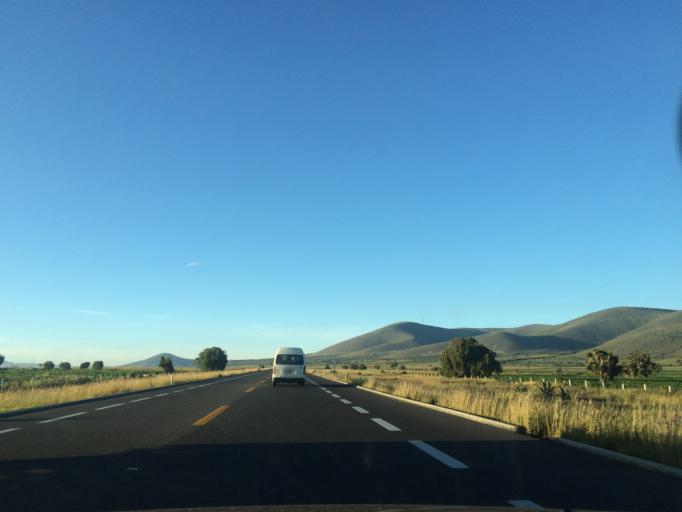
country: MX
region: Puebla
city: Morelos Canada
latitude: 18.7571
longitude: -97.4816
